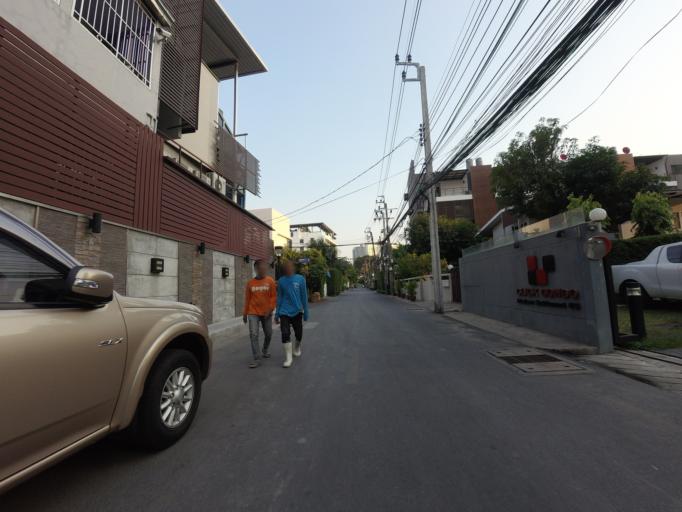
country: TH
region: Bangkok
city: Watthana
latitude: 13.7226
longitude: 100.5881
